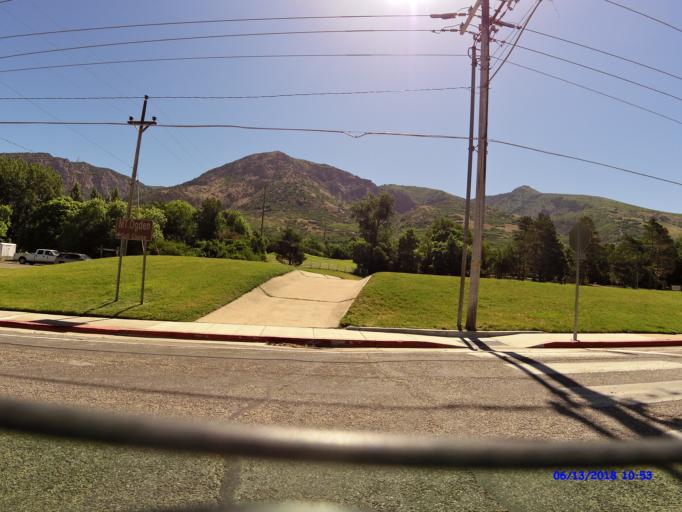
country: US
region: Utah
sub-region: Weber County
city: South Ogden
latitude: 41.2056
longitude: -111.9403
